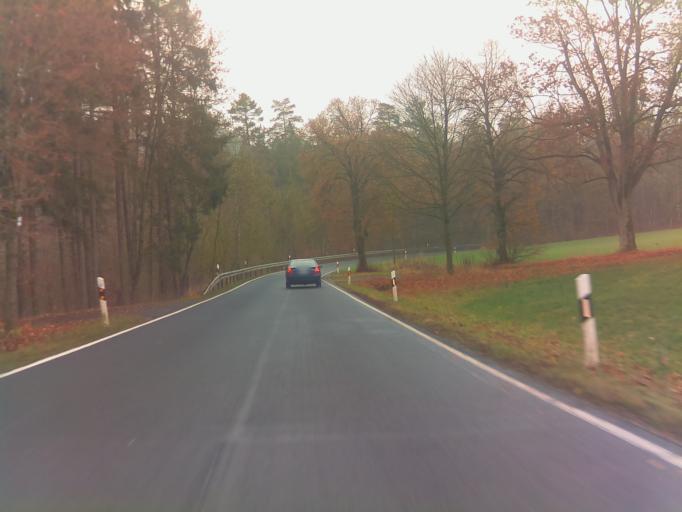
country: DE
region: Thuringia
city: Leutersdorf
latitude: 50.4763
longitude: 10.5581
